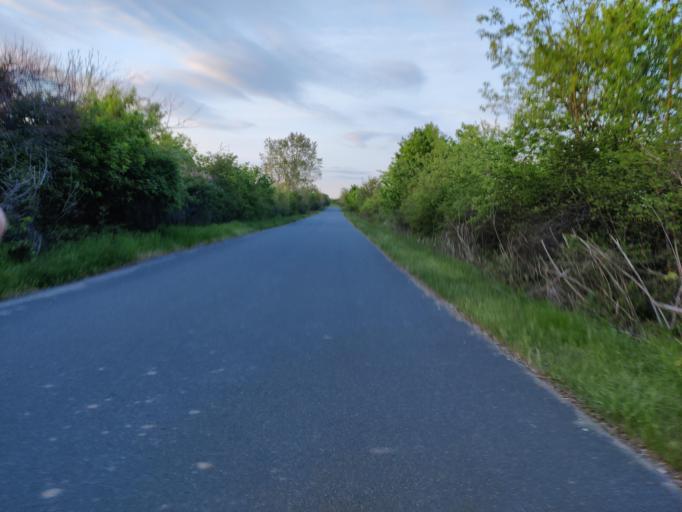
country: DE
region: Saxony
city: Bohlen
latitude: 51.2253
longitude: 12.3656
